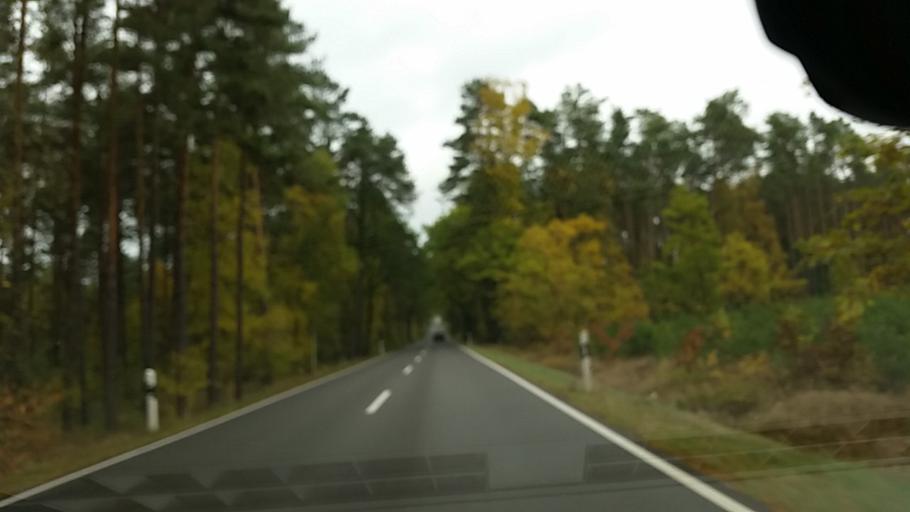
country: DE
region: Lower Saxony
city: Bergfeld
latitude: 52.6107
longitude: 10.8079
